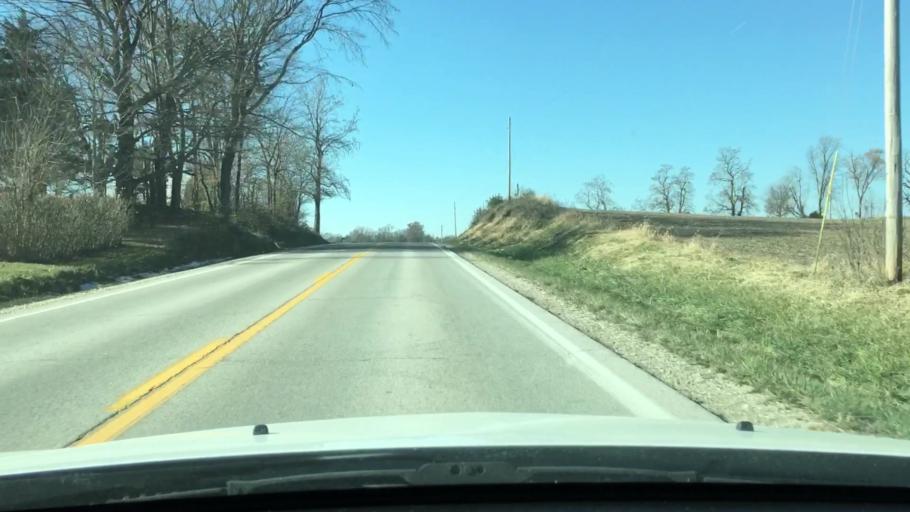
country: US
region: Illinois
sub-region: Pike County
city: Pittsfield
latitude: 39.6134
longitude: -90.7439
